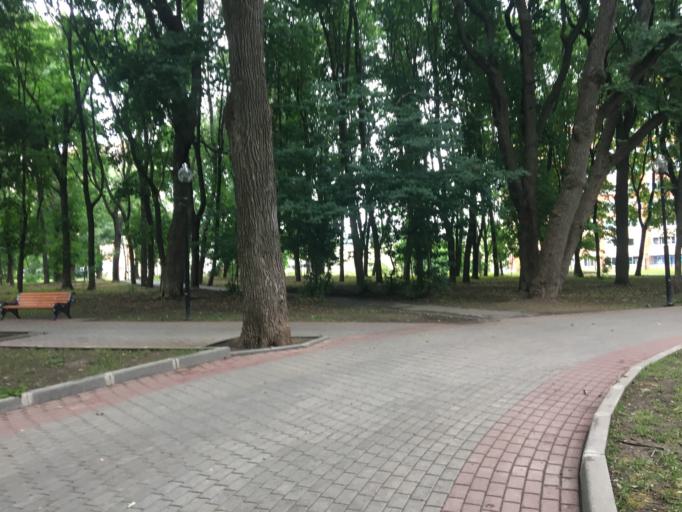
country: RU
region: Tula
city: Tula
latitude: 54.1721
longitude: 37.6159
